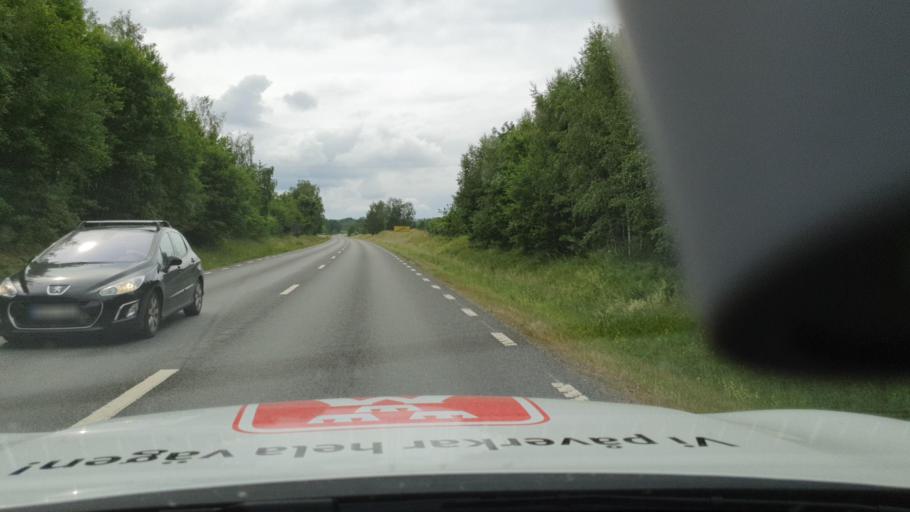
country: SE
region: Vaestra Goetaland
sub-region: Hjo Kommun
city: Hjo
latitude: 58.2265
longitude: 14.1989
